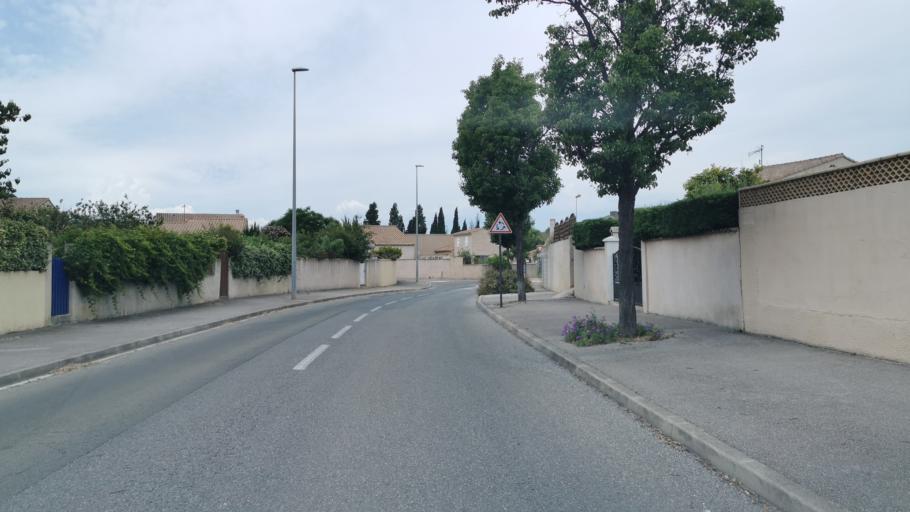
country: FR
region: Languedoc-Roussillon
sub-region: Departement de l'Aude
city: Narbonne
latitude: 43.1942
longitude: 3.0221
